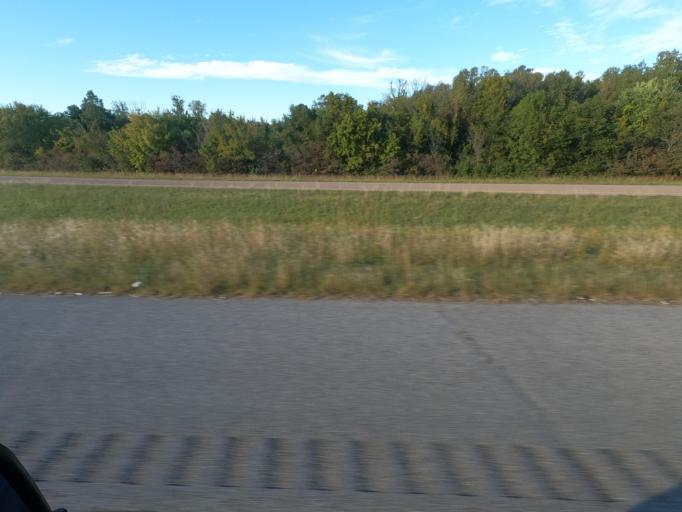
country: US
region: Tennessee
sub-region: Shelby County
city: Millington
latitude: 35.3304
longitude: -89.8956
